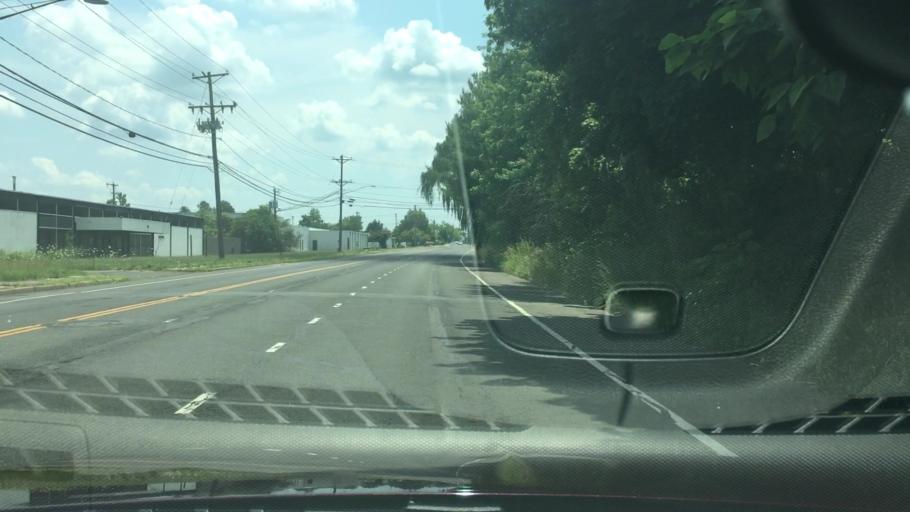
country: US
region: Connecticut
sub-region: Hartford County
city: New Britain
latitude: 41.6575
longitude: -72.7534
